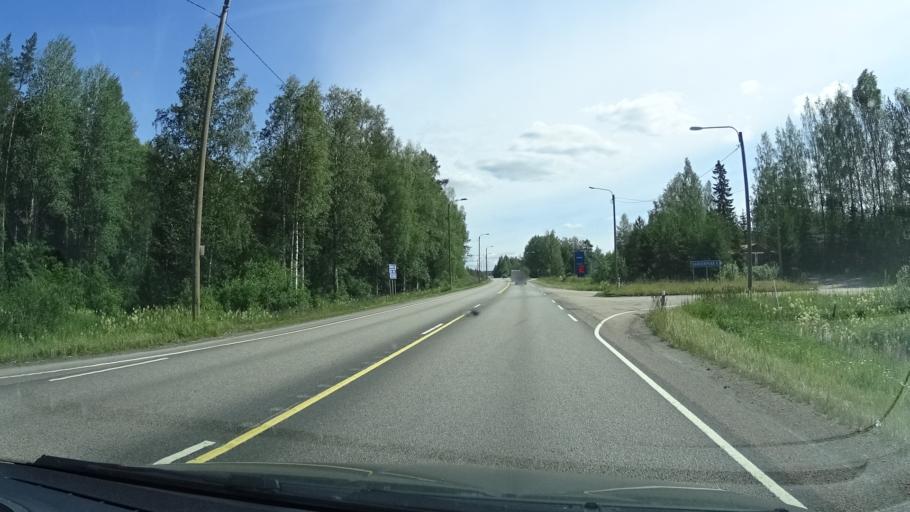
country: FI
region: Central Finland
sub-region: Jyvaeskylae
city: Uurainen
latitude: 62.2662
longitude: 25.4447
